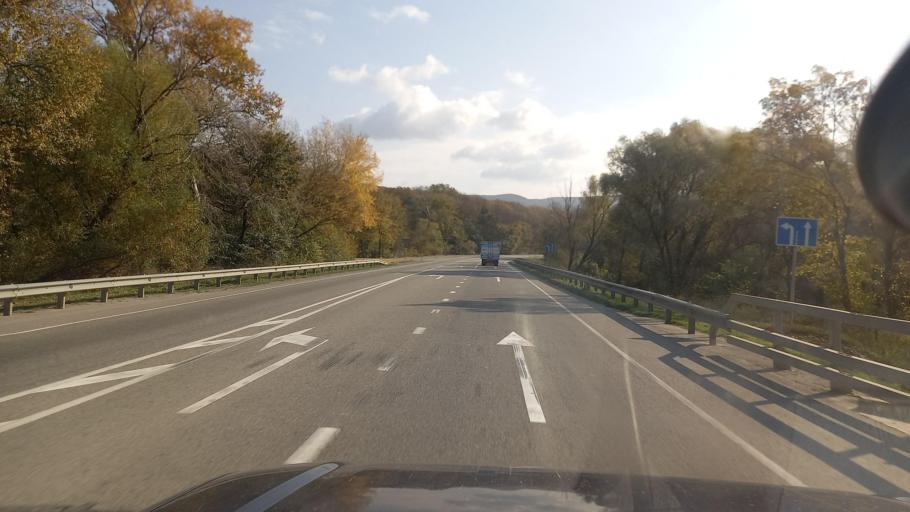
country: RU
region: Krasnodarskiy
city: Verkhnebakanskiy
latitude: 44.8434
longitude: 37.6939
